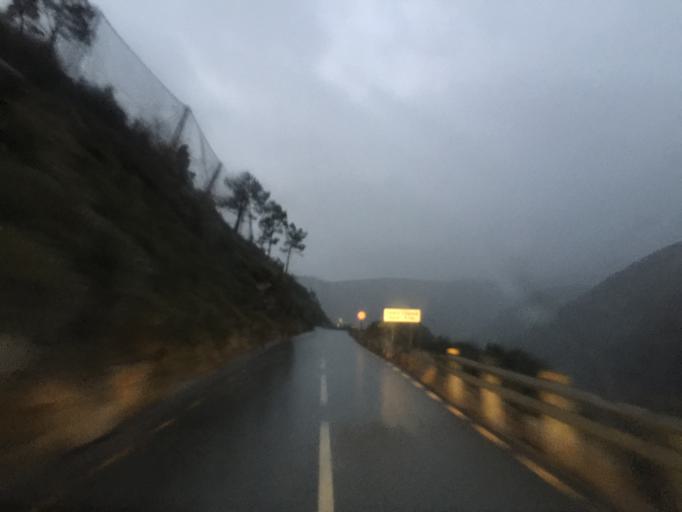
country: PT
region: Guarda
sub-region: Manteigas
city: Manteigas
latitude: 40.3390
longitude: -7.5666
